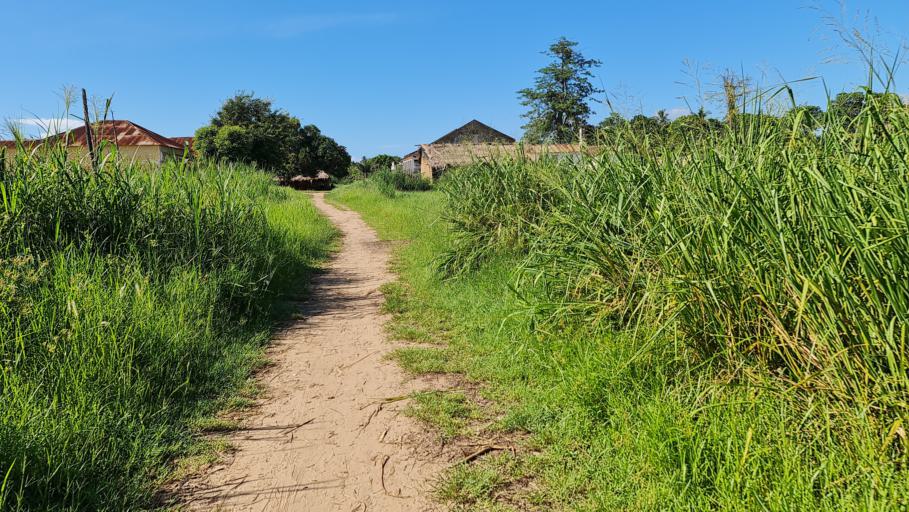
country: MZ
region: Zambezia
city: Quelimane
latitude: -17.4435
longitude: 37.6988
